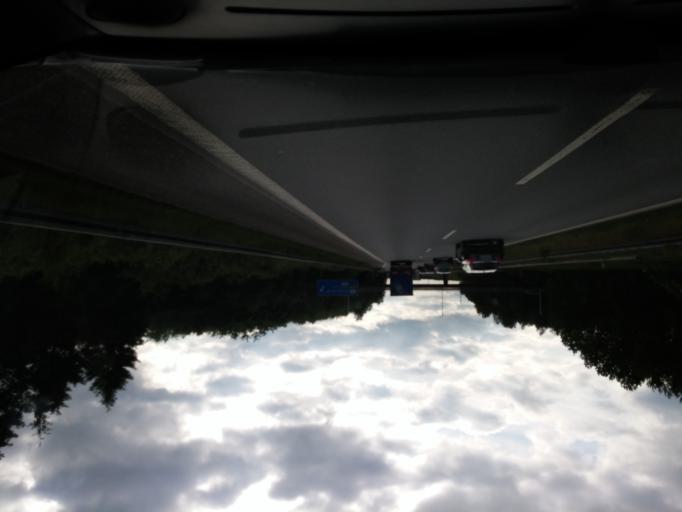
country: DK
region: Zealand
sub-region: Ringsted Kommune
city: Ringsted
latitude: 55.4558
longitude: 11.8288
